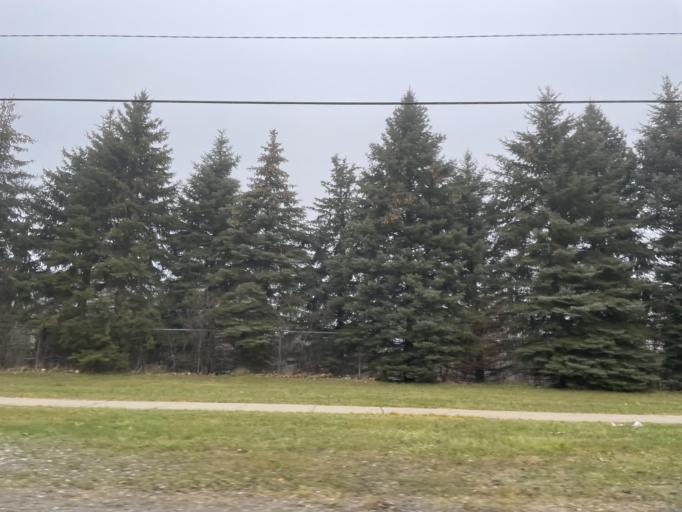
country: CA
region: Ontario
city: Kitchener
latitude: 43.4421
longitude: -80.4169
